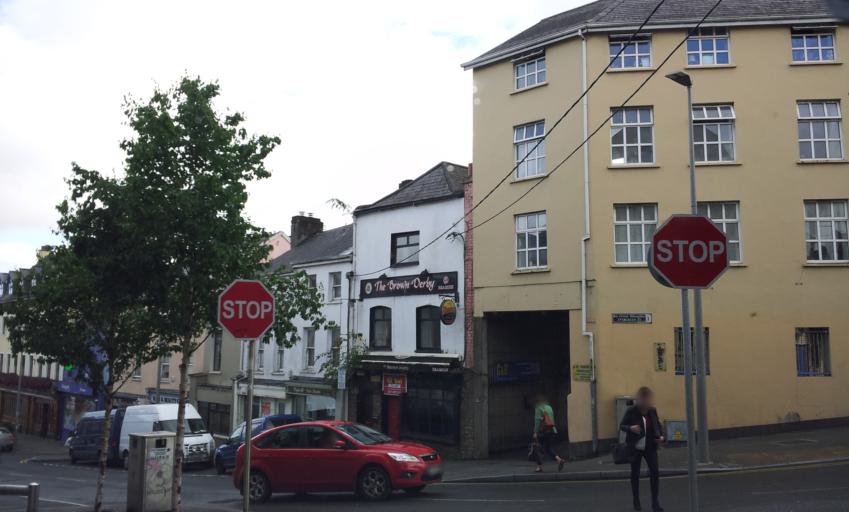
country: IE
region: Munster
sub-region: County Cork
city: Cork
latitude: 51.8945
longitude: -8.4764
